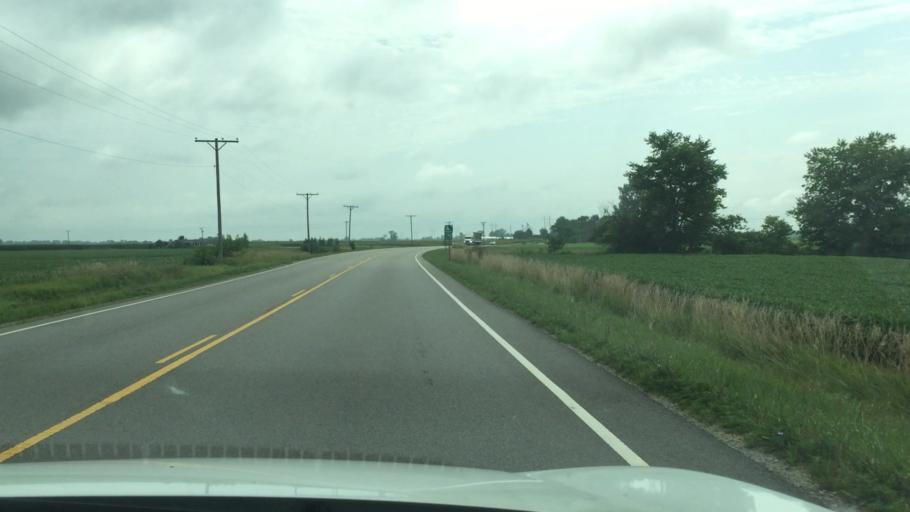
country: US
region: Ohio
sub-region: Champaign County
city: North Lewisburg
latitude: 40.1499
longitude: -83.4615
